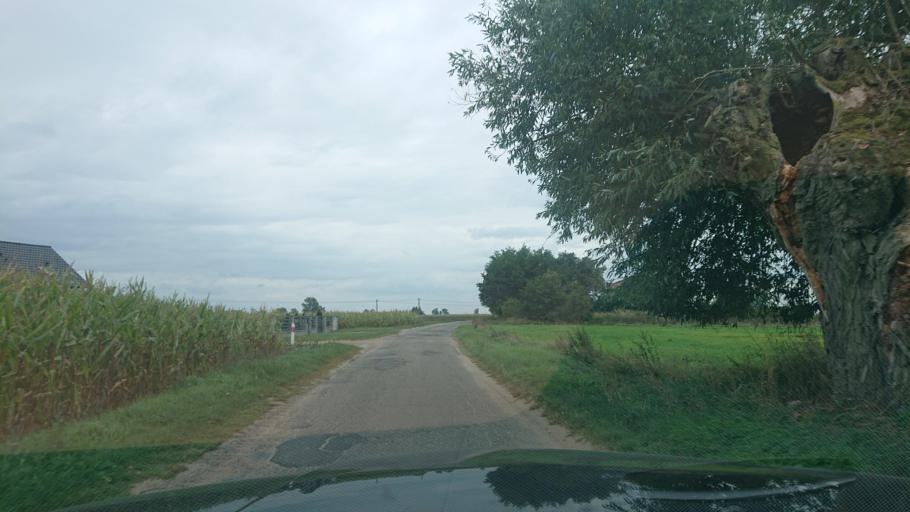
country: PL
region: Greater Poland Voivodeship
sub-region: Powiat gnieznienski
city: Niechanowo
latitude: 52.4788
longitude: 17.6195
